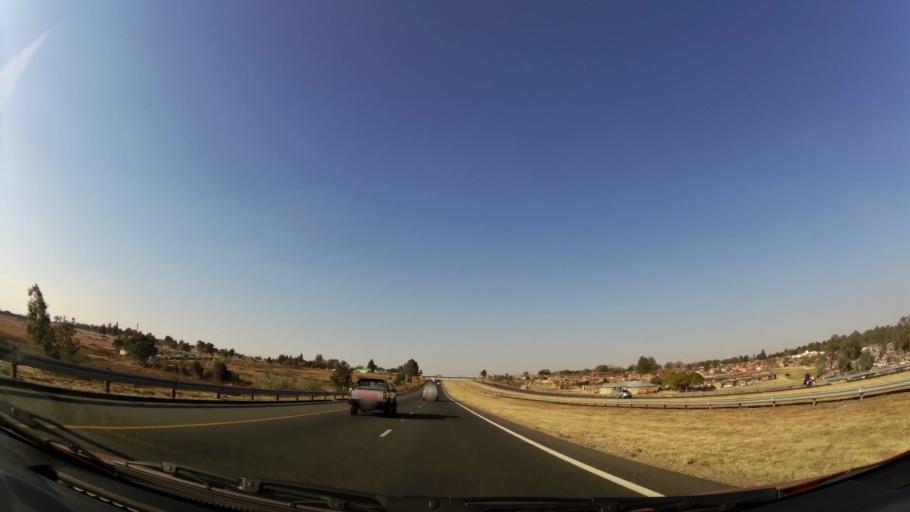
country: ZA
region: Gauteng
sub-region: West Rand District Municipality
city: Muldersdriseloop
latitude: -26.0148
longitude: 27.8737
